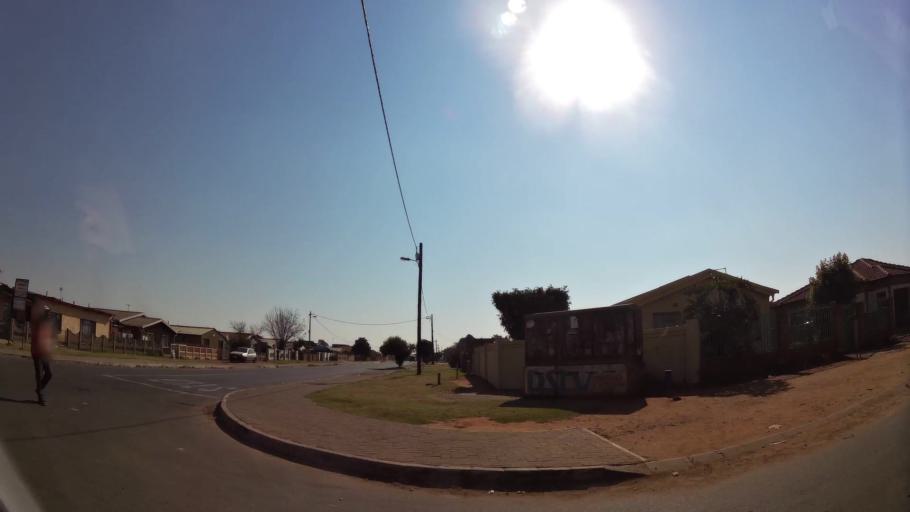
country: ZA
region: Gauteng
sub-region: Ekurhuleni Metropolitan Municipality
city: Boksburg
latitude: -26.2201
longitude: 28.2962
